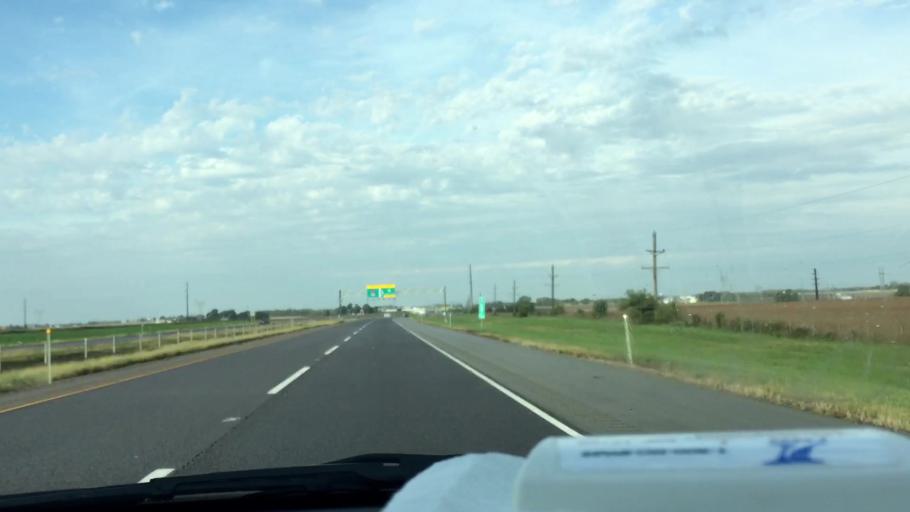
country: US
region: Illinois
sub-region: Lee County
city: Dixon
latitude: 41.8229
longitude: -89.4004
